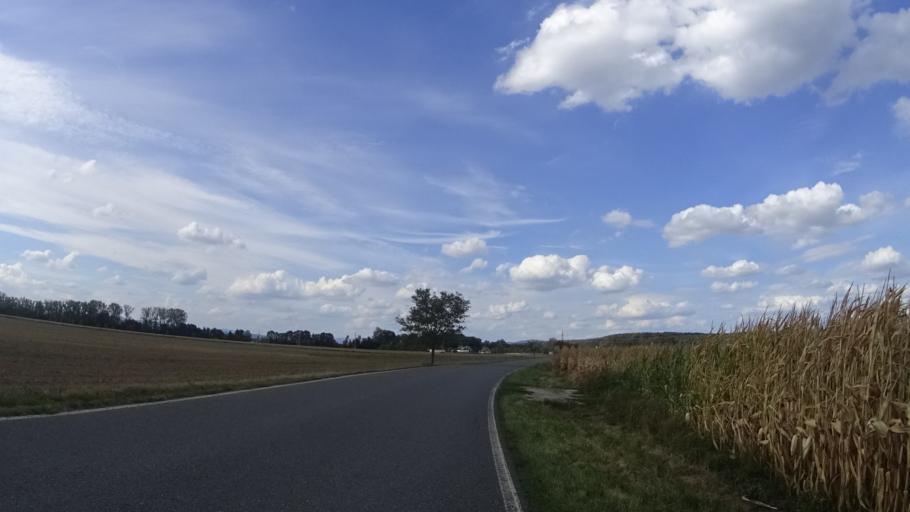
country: CZ
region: Olomoucky
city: Moravicany
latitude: 49.7371
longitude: 16.9737
